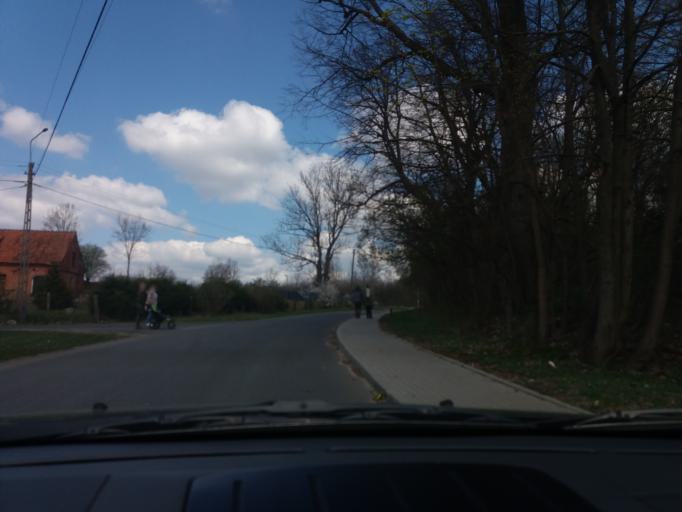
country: PL
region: Warmian-Masurian Voivodeship
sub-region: Powiat nidzicki
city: Nidzica
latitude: 53.3743
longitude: 20.6056
